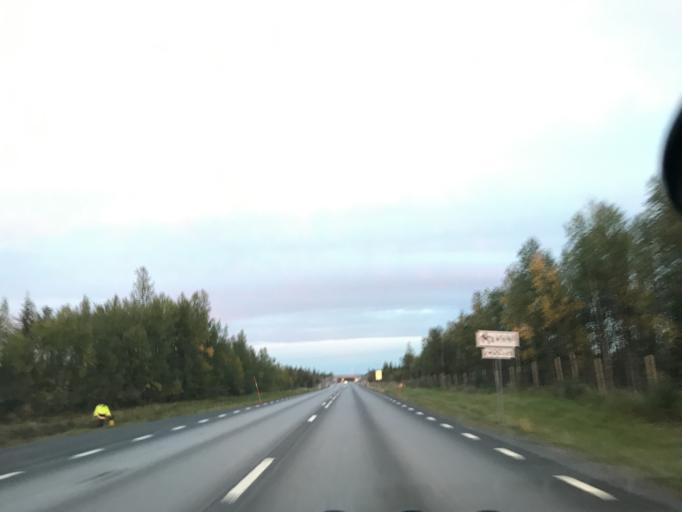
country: SE
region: Norrbotten
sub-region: Gallivare Kommun
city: Malmberget
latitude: 67.6960
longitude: 20.7980
